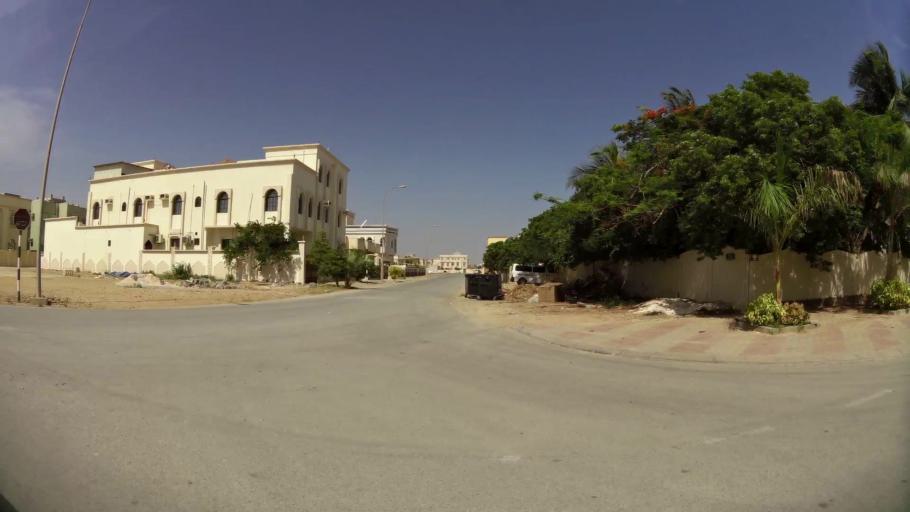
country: OM
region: Zufar
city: Salalah
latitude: 17.0472
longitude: 54.1496
